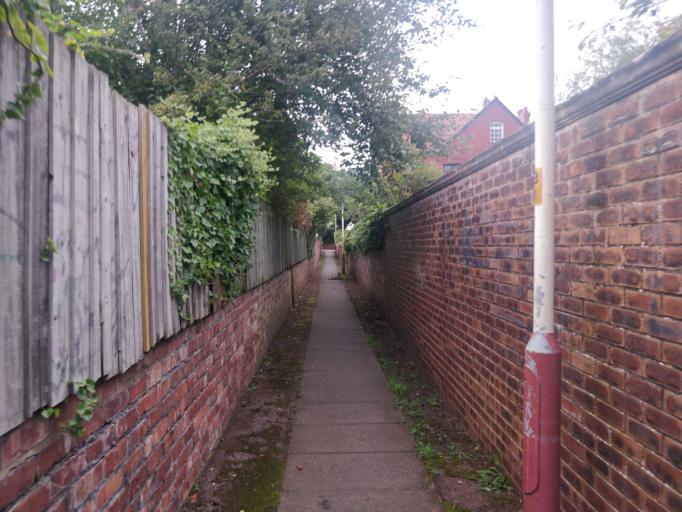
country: GB
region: England
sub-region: Sefton
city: Southport
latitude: 53.6596
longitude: -2.9733
